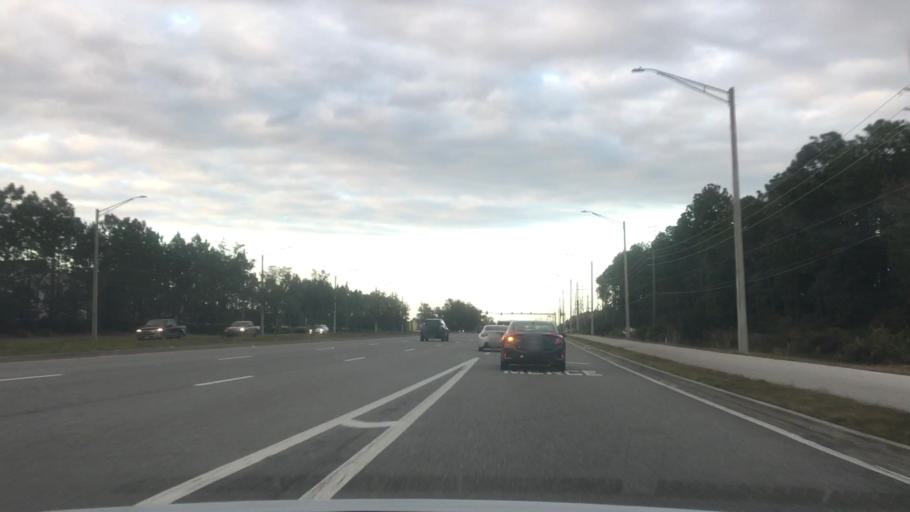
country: US
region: Florida
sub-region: Duval County
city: Neptune Beach
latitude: 30.2922
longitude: -81.4887
